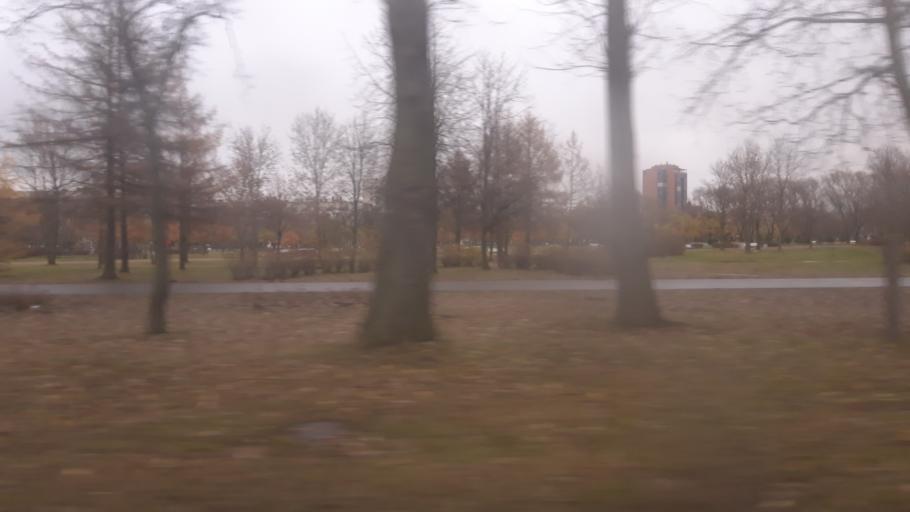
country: RU
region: St.-Petersburg
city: Kupchino
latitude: 59.8393
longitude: 30.3225
